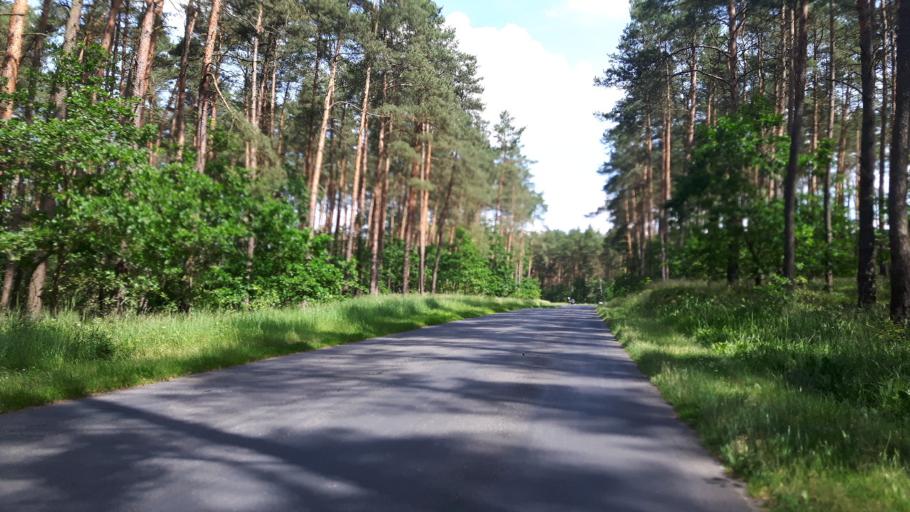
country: PL
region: West Pomeranian Voivodeship
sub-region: Powiat goleniowski
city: Goleniow
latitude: 53.5121
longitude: 14.7879
